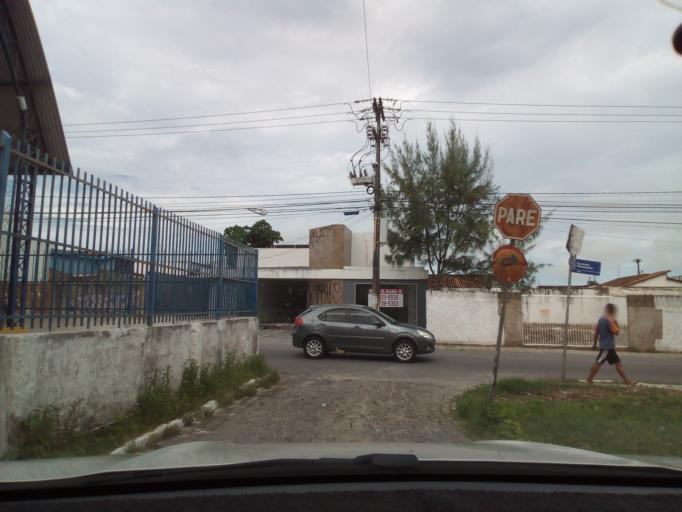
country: BR
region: Paraiba
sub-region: Joao Pessoa
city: Joao Pessoa
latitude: -7.1216
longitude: -34.8625
